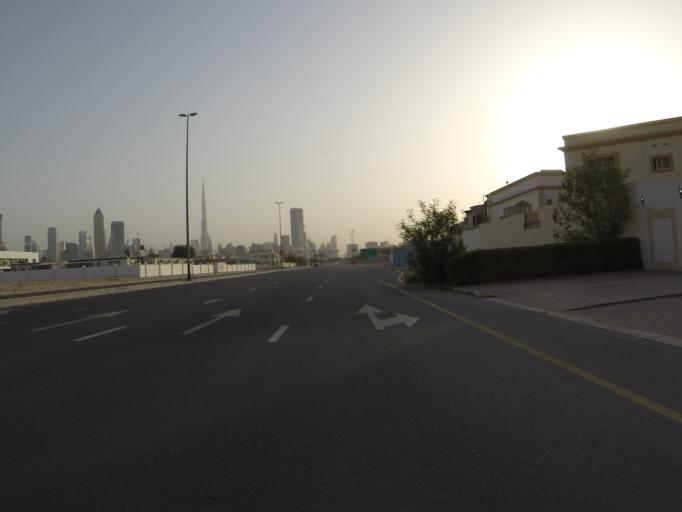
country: AE
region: Dubai
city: Dubai
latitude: 25.1649
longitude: 55.2591
